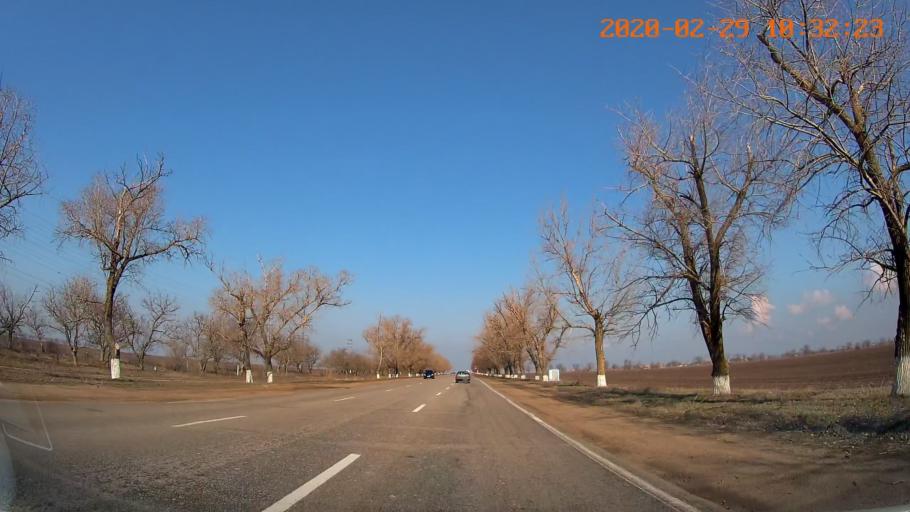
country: UA
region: Odessa
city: Velykoploske
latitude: 46.9604
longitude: 29.5543
